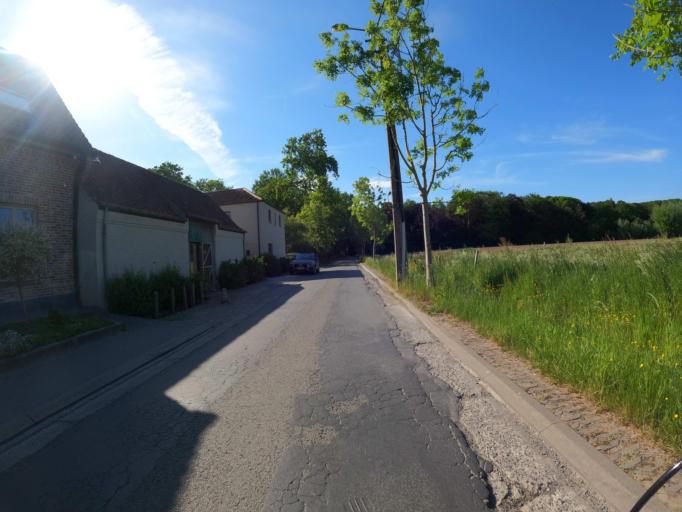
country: BE
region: Flanders
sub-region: Provincie Oost-Vlaanderen
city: Merelbeke
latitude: 50.9555
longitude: 3.7259
